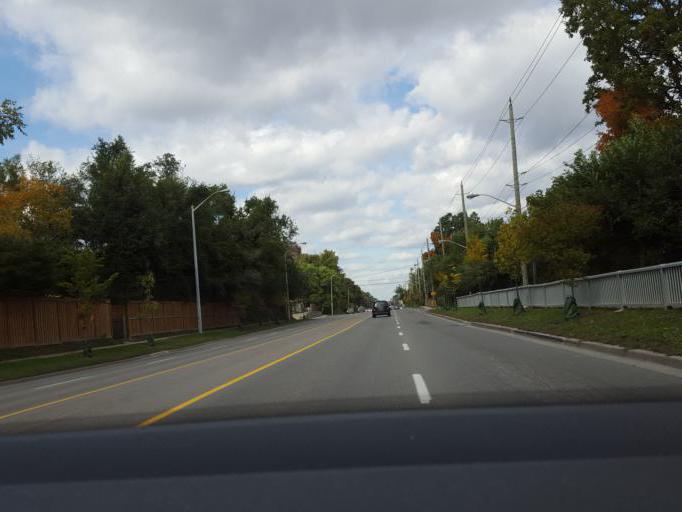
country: CA
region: Ontario
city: Willowdale
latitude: 43.7487
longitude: -79.3592
